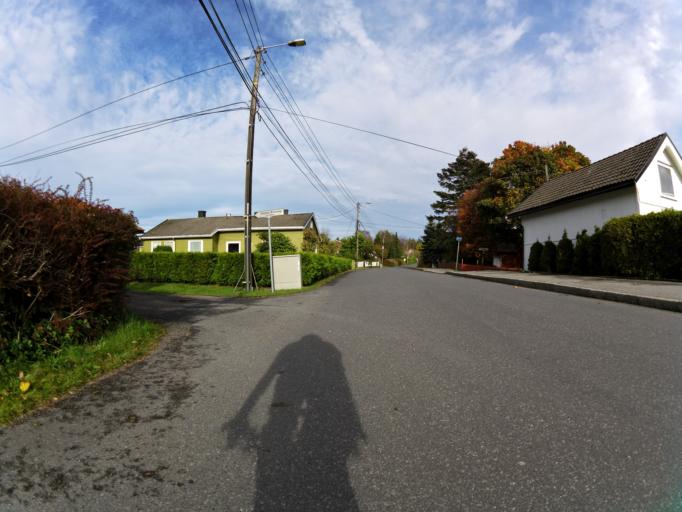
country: NO
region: Ostfold
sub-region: Fredrikstad
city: Fredrikstad
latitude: 59.2336
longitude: 10.9653
